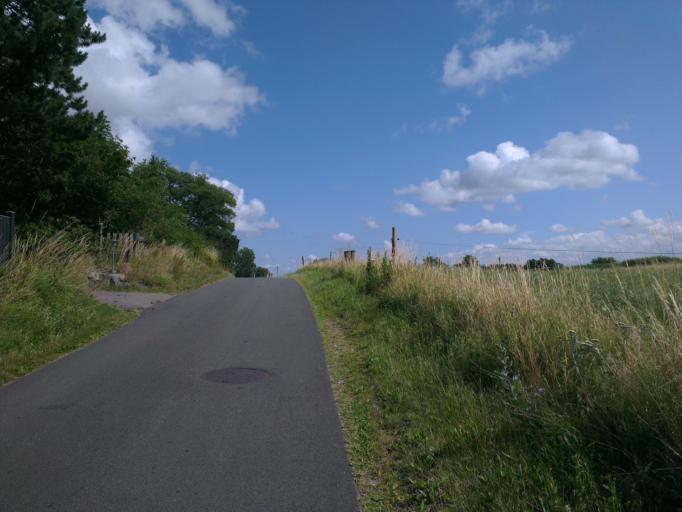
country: DK
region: Zealand
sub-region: Lejre Kommune
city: Ejby
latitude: 55.7420
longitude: 11.8721
